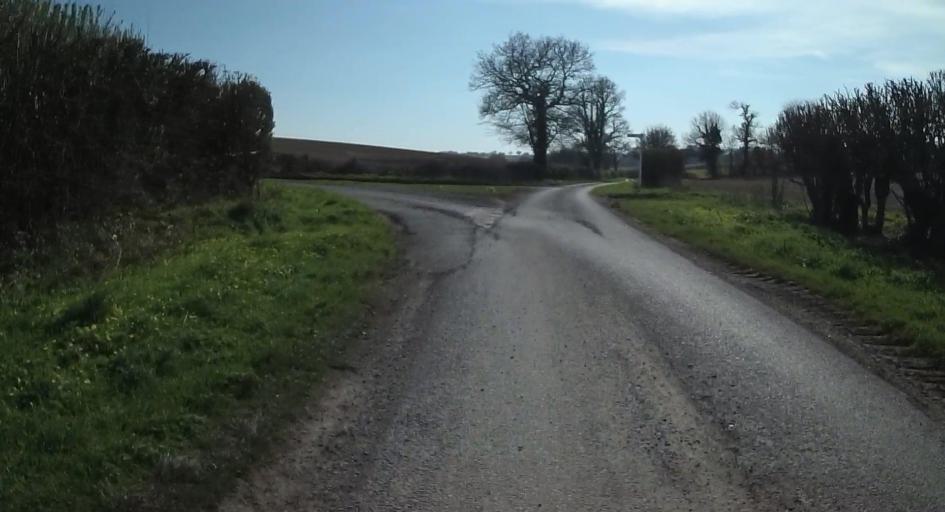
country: GB
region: England
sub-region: Hampshire
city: Highclere
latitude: 51.2655
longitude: -1.3915
